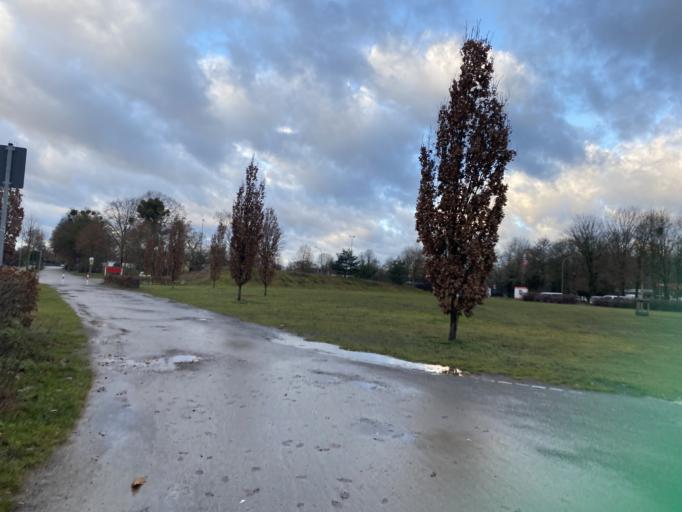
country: DE
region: North Rhine-Westphalia
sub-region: Regierungsbezirk Arnsberg
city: Hamm
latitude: 51.6894
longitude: 7.8378
